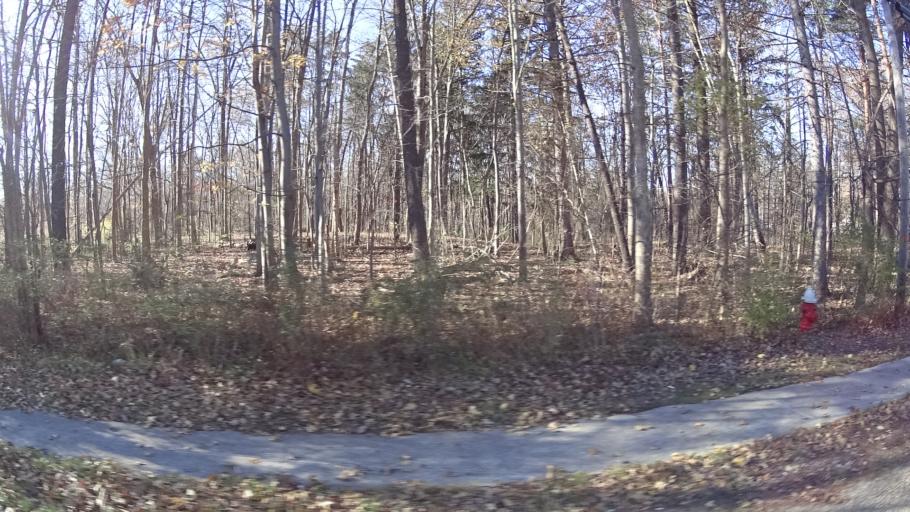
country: US
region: Ohio
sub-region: Lorain County
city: Avon
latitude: 41.4460
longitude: -82.0306
